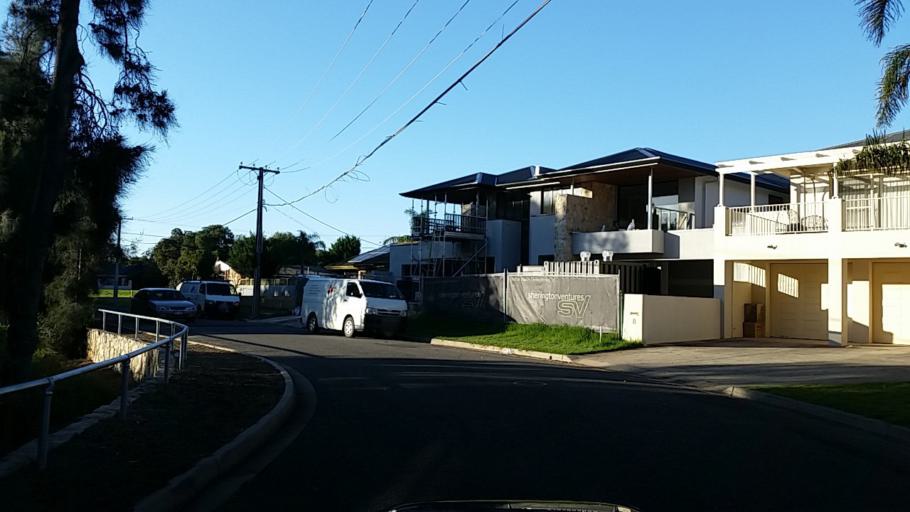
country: AU
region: South Australia
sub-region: Charles Sturt
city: Grange
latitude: -34.9057
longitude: 138.5000
